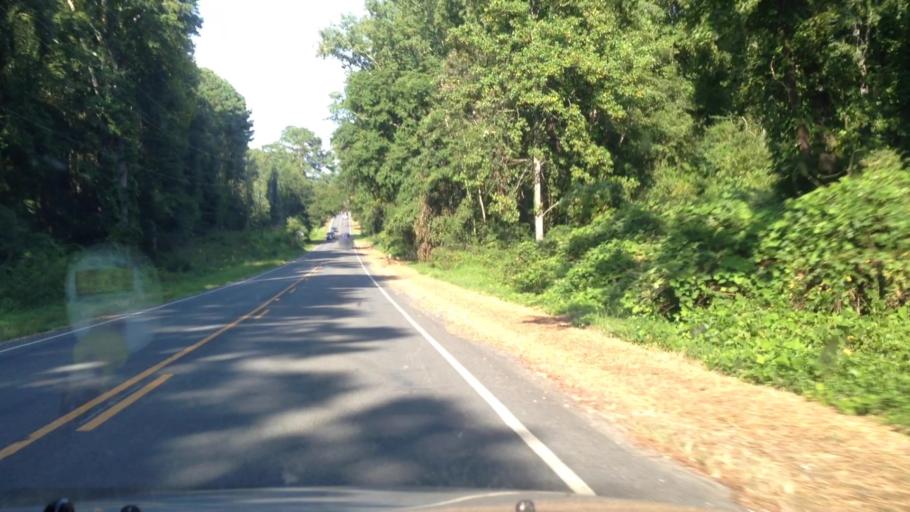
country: US
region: North Carolina
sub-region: Harnett County
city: Buies Creek
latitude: 35.4087
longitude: -78.7319
